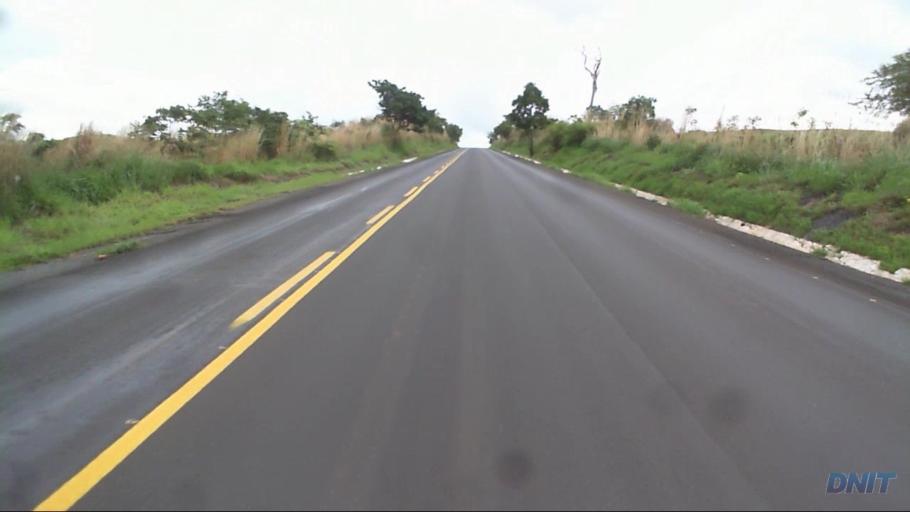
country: BR
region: Goias
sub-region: Padre Bernardo
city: Padre Bernardo
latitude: -15.2142
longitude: -48.4986
